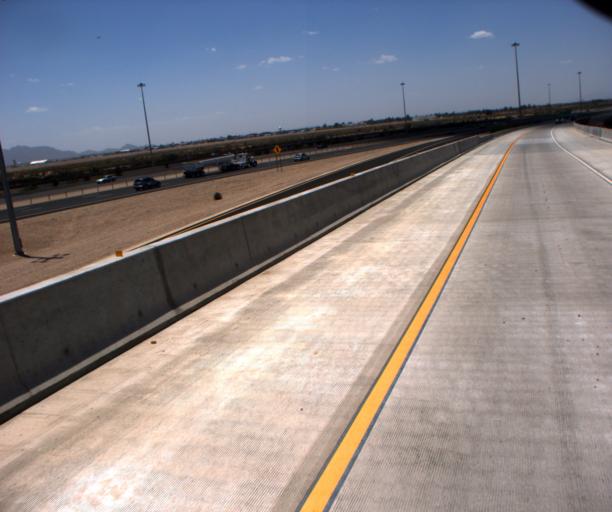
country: US
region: Arizona
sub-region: Maricopa County
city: Queen Creek
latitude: 33.3311
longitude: -111.6559
